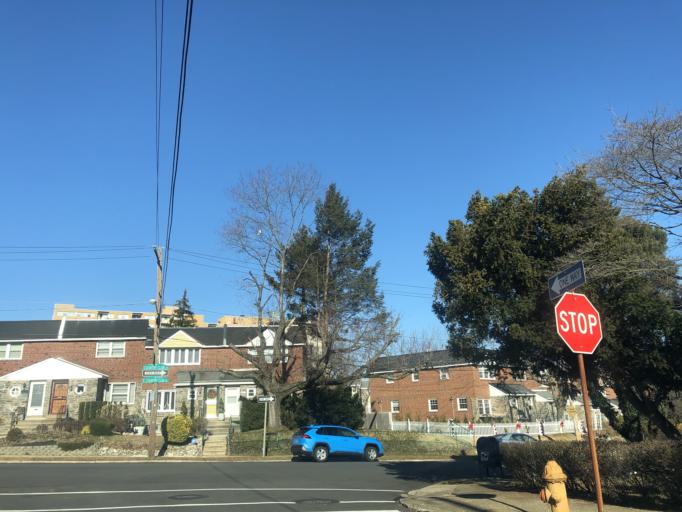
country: US
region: Pennsylvania
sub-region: Montgomery County
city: Bala-Cynwyd
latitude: 40.0017
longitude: -75.2038
